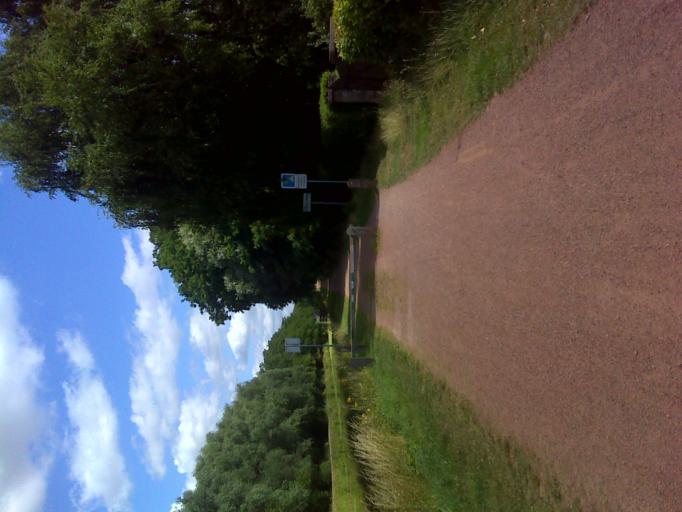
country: FR
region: Nord-Pas-de-Calais
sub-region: Departement du Nord
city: Wasquehal
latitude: 50.6762
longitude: 3.1269
